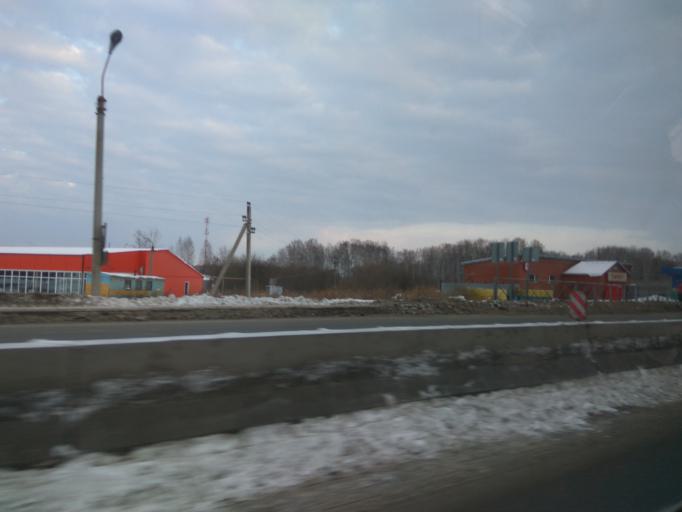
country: RU
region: Novosibirsk
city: Bolotnoye
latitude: 55.6463
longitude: 84.3596
